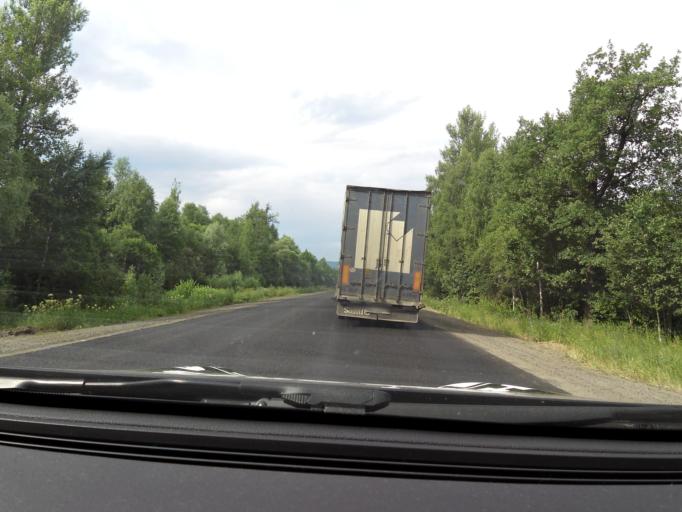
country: RU
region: Chelyabinsk
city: Asha
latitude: 54.8626
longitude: 57.1624
